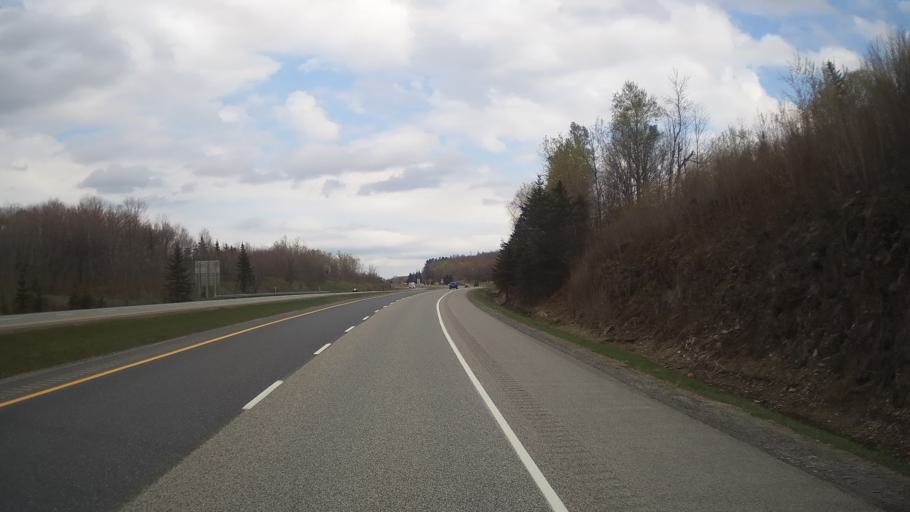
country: CA
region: Quebec
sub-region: Estrie
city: Magog
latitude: 45.2971
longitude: -72.3030
